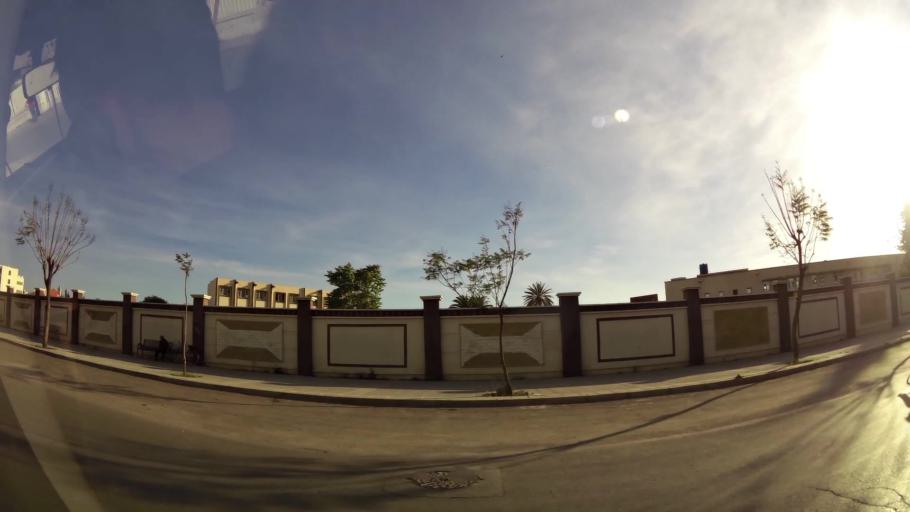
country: MA
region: Oriental
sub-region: Oujda-Angad
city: Oujda
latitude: 34.6756
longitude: -1.9155
